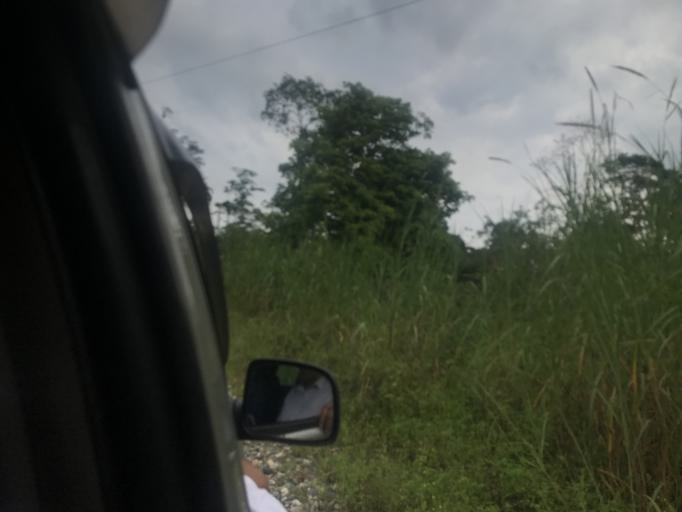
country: EC
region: Napo
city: Tena
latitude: -1.0202
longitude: -77.7416
